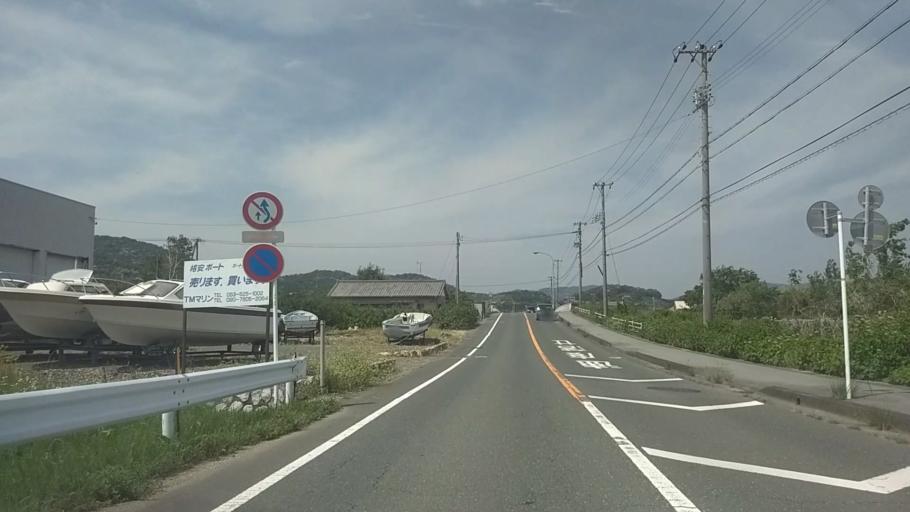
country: JP
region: Shizuoka
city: Kosai-shi
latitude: 34.7807
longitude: 137.5416
